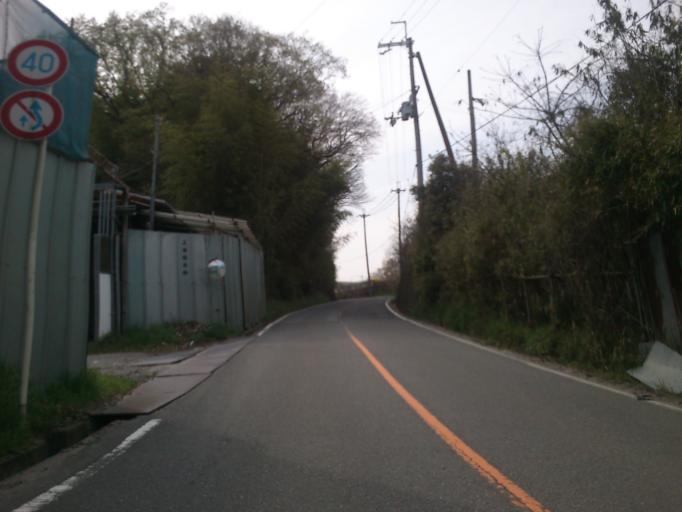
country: JP
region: Kyoto
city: Tanabe
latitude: 34.7904
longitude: 135.7478
